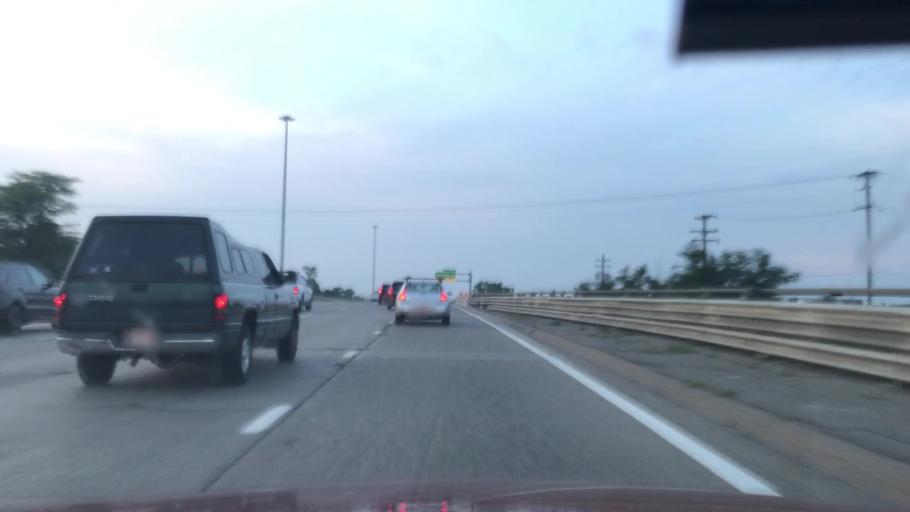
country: US
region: Michigan
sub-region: Kent County
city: Grand Rapids
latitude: 42.9760
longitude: -85.6775
